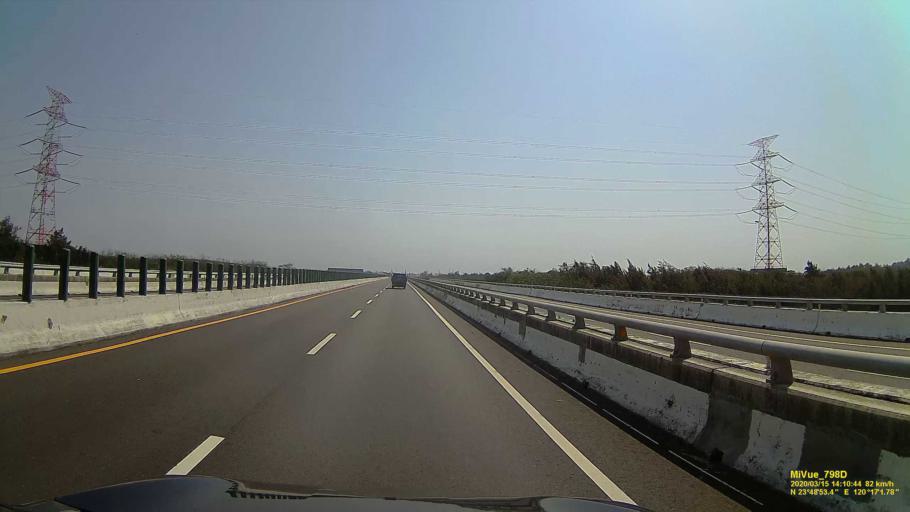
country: TW
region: Taiwan
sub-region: Yunlin
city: Douliu
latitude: 23.8140
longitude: 120.2835
